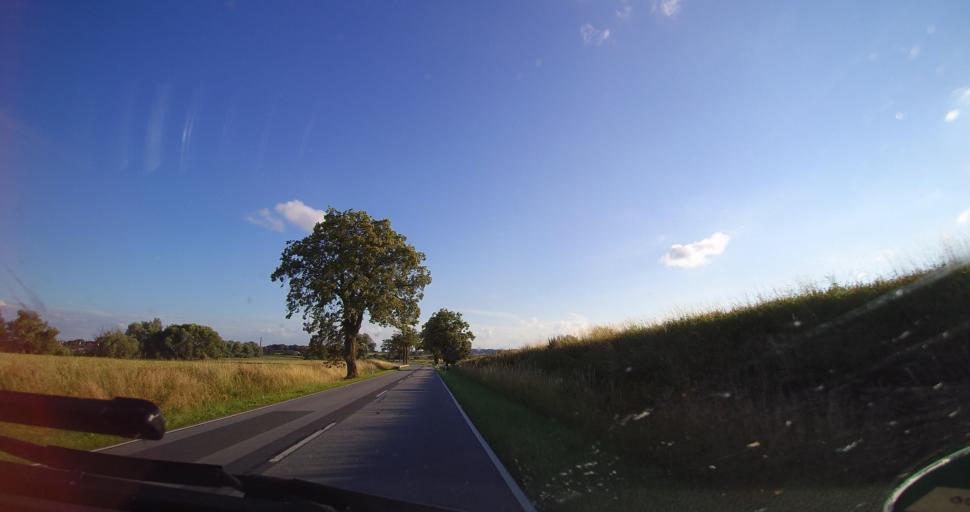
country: DE
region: Mecklenburg-Vorpommern
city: Tribsees
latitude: 54.1032
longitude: 12.7554
